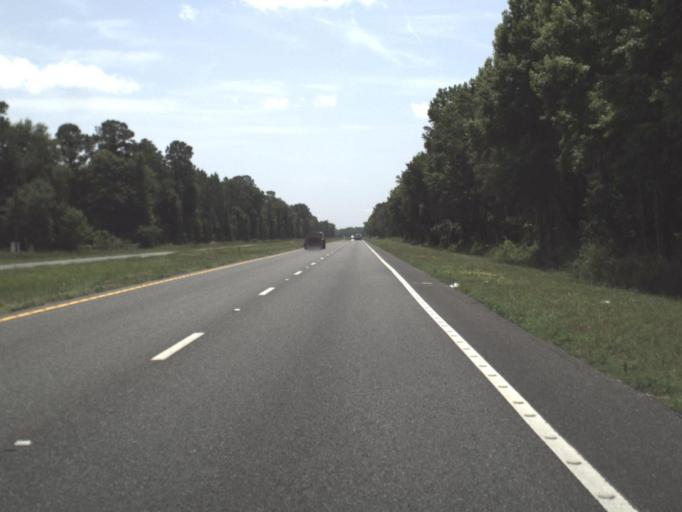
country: US
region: Florida
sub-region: Taylor County
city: Perry
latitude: 29.9762
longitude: -83.4855
